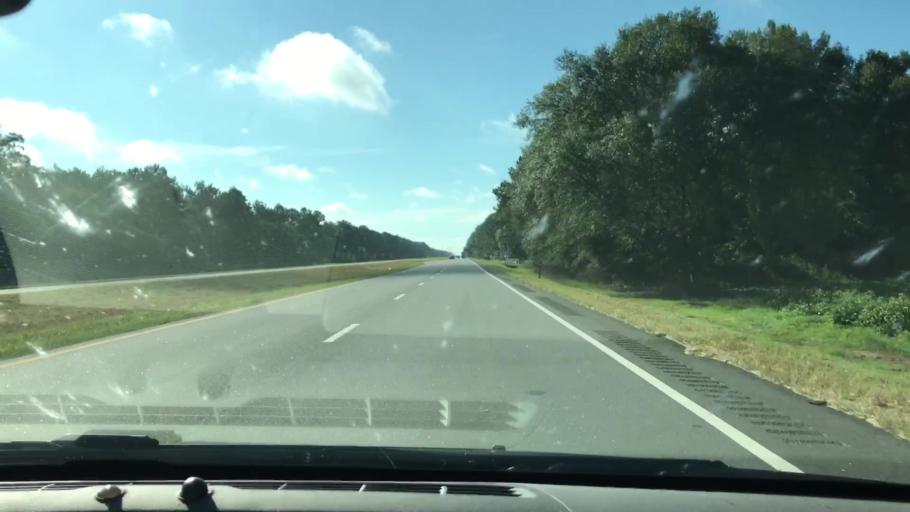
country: US
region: Georgia
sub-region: Lee County
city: Leesburg
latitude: 31.6870
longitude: -84.3080
